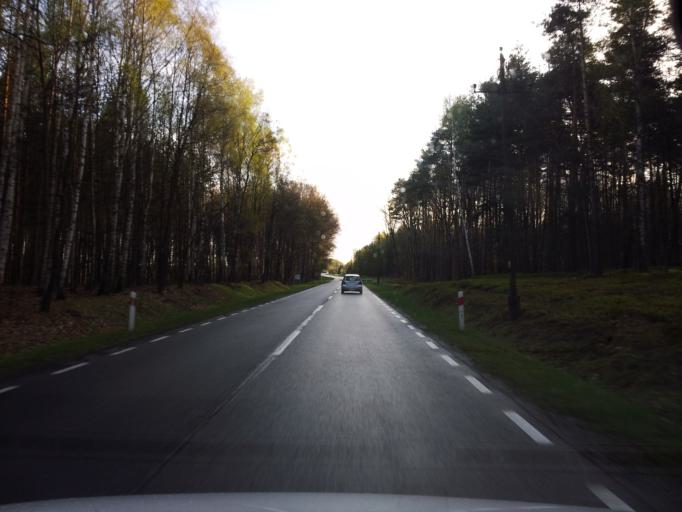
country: PL
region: Lubusz
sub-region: Powiat zarski
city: Sieniawa Zarska
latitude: 51.5910
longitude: 15.0846
